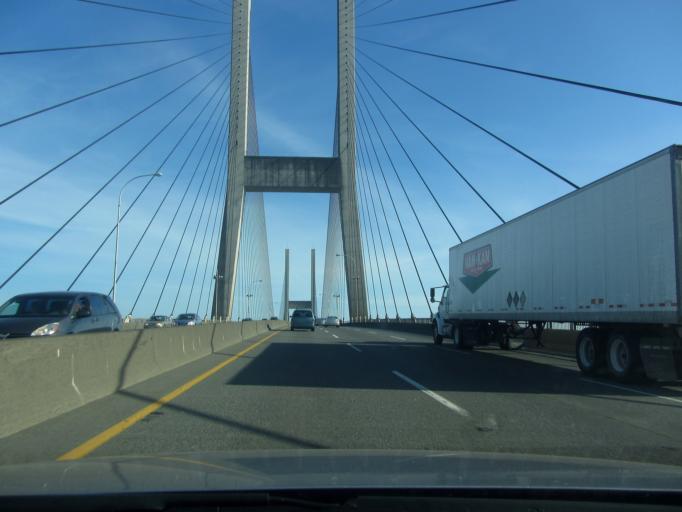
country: CA
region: British Columbia
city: Delta
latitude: 49.1627
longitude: -122.9441
